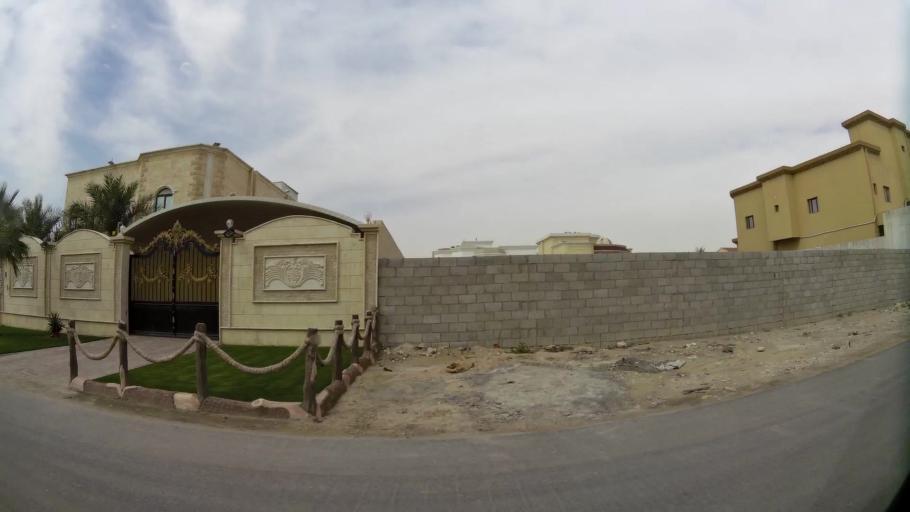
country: QA
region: Baladiyat ad Dawhah
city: Doha
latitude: 25.2154
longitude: 51.4764
